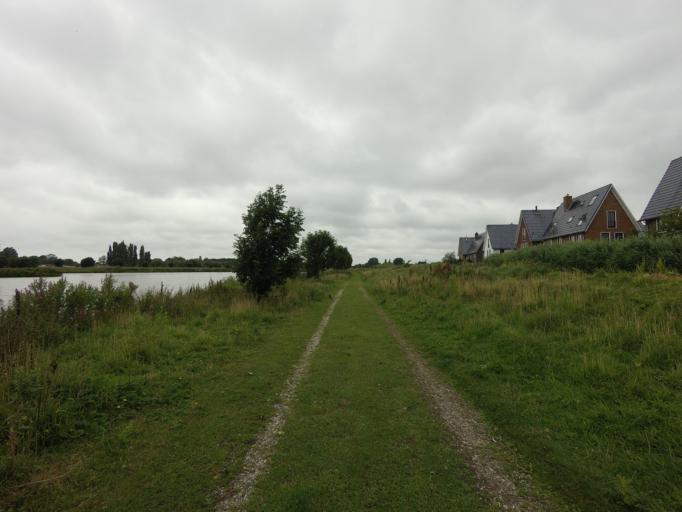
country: NL
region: South Holland
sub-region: Gemeente Leiden
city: Leiden
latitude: 52.1830
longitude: 4.4949
